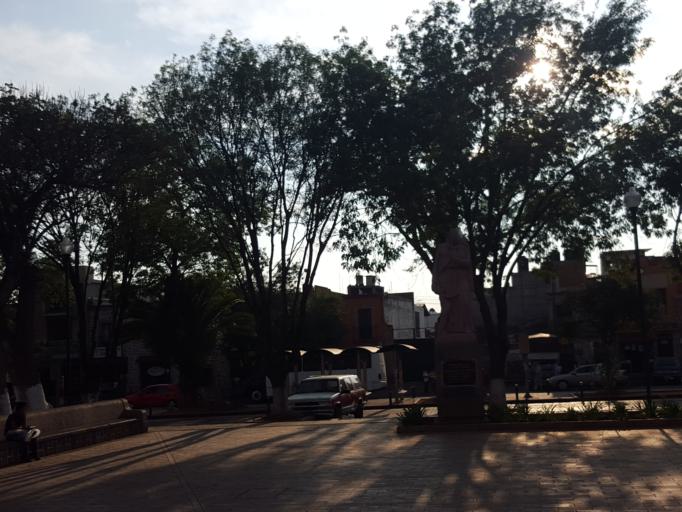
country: MX
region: Michoacan
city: Morelia
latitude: 19.6964
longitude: -101.1948
